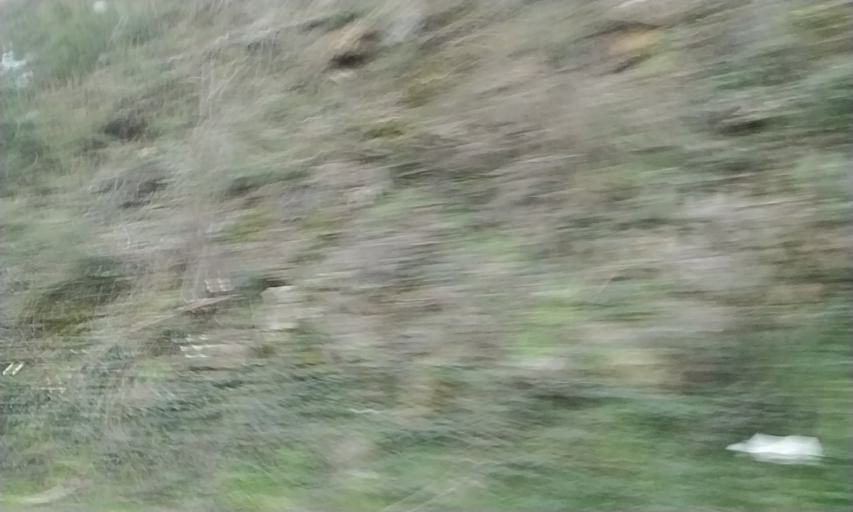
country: PT
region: Vila Real
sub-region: Mondim de Basto
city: Mondim de Basto
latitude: 41.4485
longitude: -7.9636
